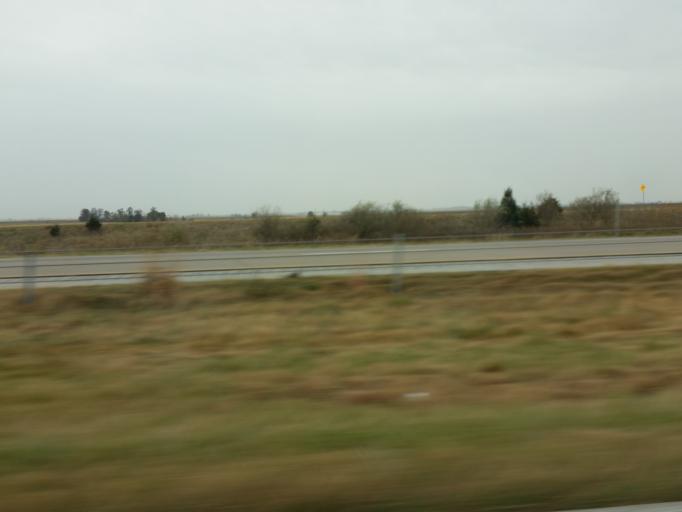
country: US
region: Iowa
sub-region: Scott County
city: Walcott
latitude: 41.6244
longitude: -90.8116
